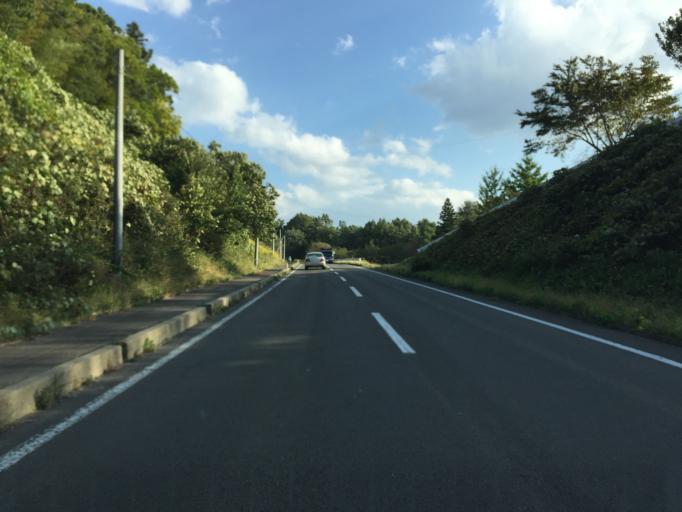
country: JP
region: Fukushima
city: Fukushima-shi
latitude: 37.6760
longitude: 140.5062
